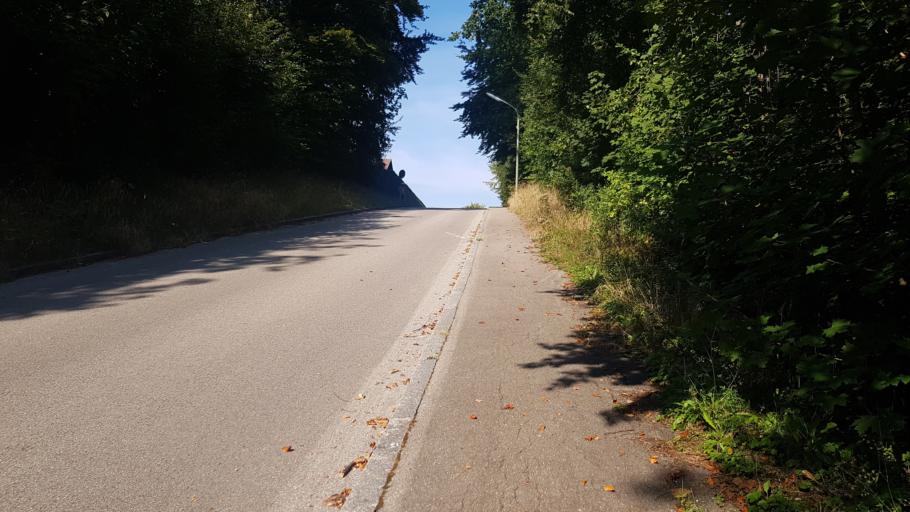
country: DE
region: Bavaria
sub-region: Upper Bavaria
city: Worthsee
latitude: 48.0643
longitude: 11.2145
